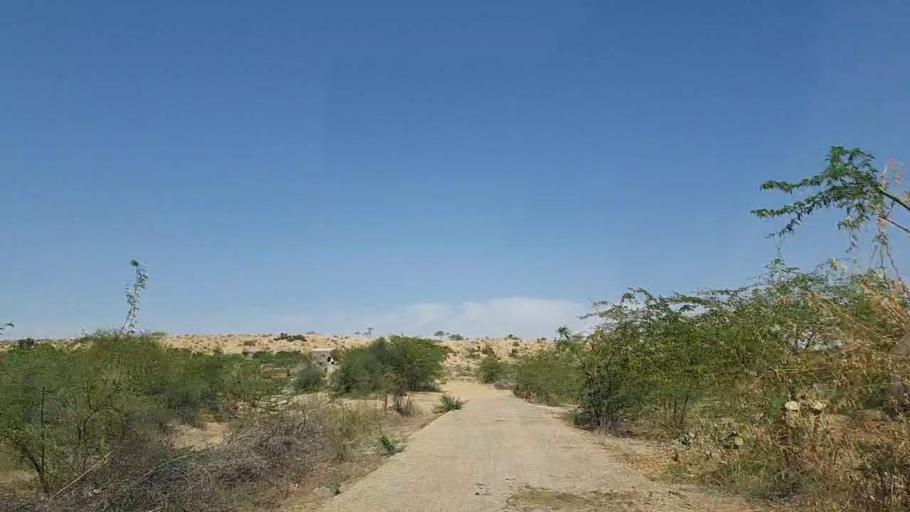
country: PK
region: Sindh
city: Mithi
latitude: 24.7897
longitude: 69.7652
